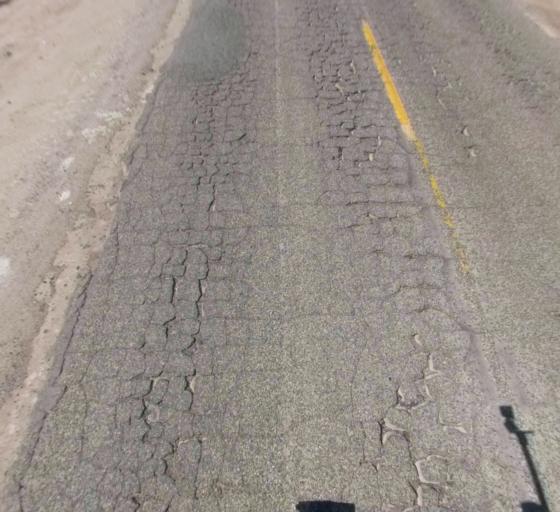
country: US
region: California
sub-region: Madera County
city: Parkwood
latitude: 36.9126
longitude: -120.0194
